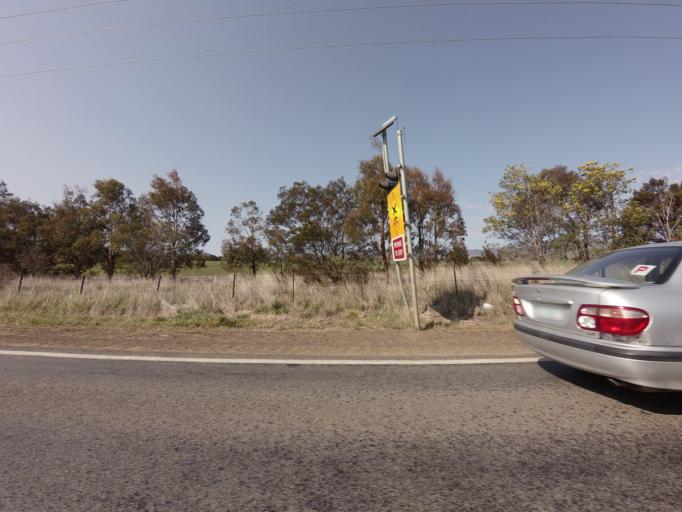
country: AU
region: Tasmania
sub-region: Northern Midlands
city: Evandale
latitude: -41.7960
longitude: 147.7073
